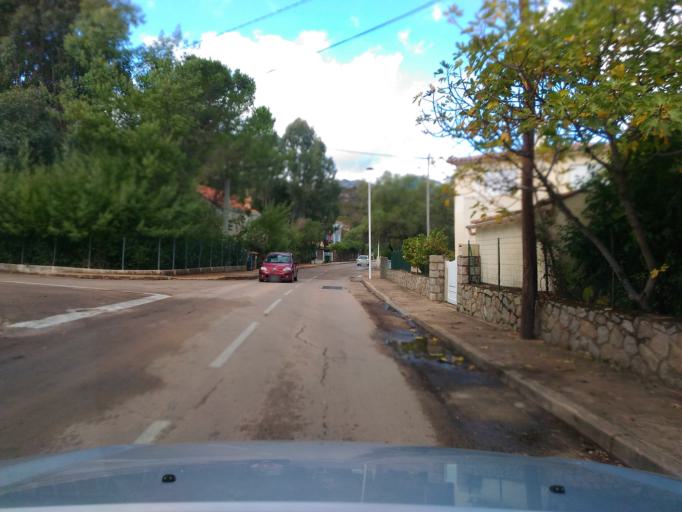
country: FR
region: Corsica
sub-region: Departement de la Corse-du-Sud
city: Porto-Vecchio
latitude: 41.7007
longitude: 9.3421
